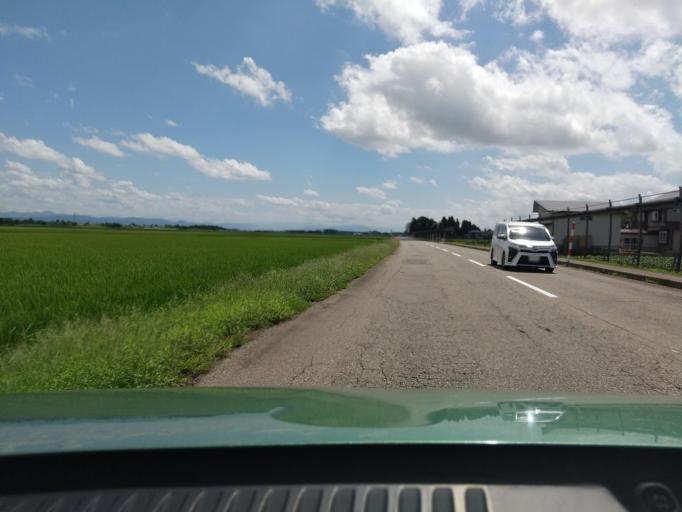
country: JP
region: Akita
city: Omagari
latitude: 39.3933
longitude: 140.4733
